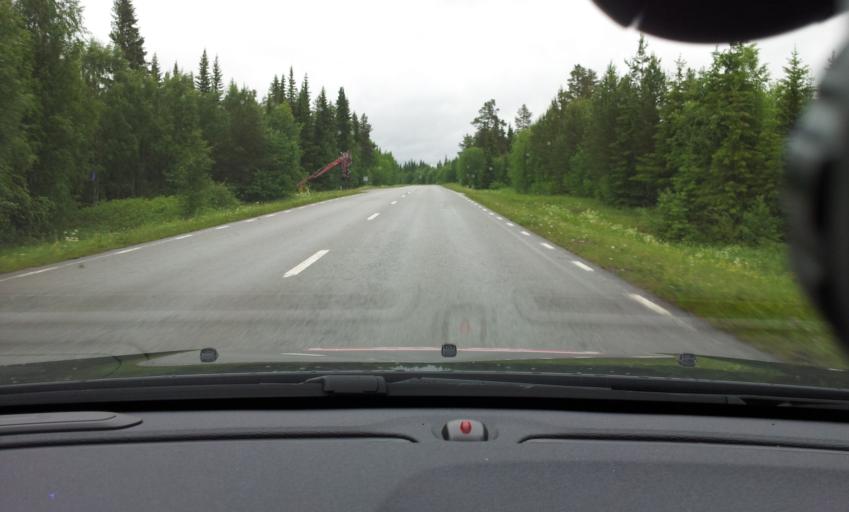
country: SE
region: Jaemtland
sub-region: Krokoms Kommun
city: Krokom
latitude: 63.4267
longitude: 14.4972
